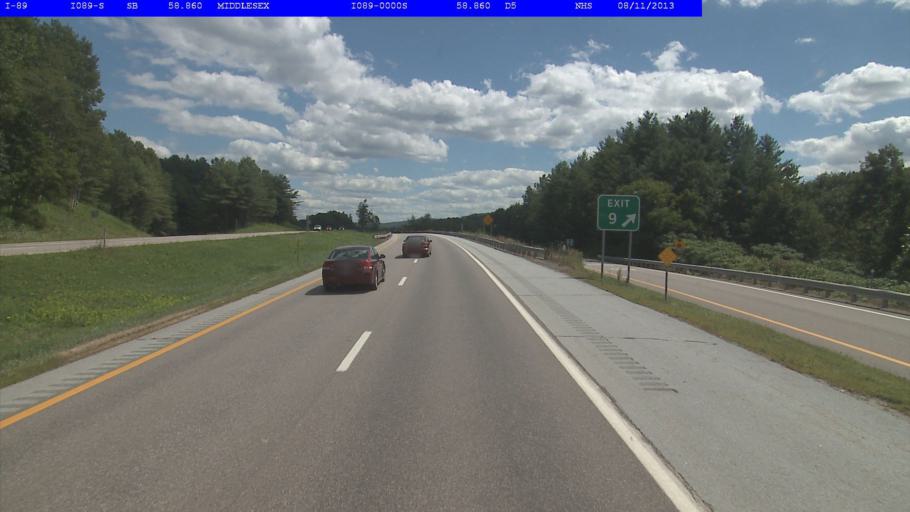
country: US
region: Vermont
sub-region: Washington County
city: Waterbury
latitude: 44.2998
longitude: -72.6874
